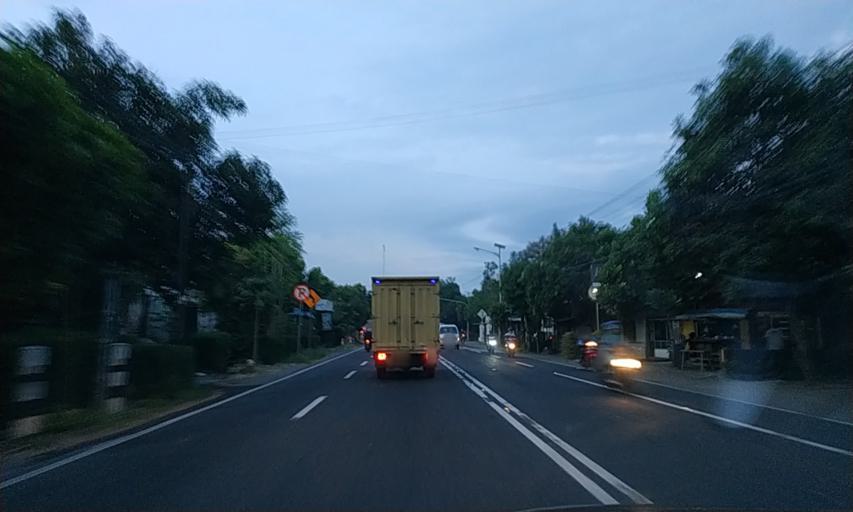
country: ID
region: Daerah Istimewa Yogyakarta
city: Godean
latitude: -7.8404
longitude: 110.2195
